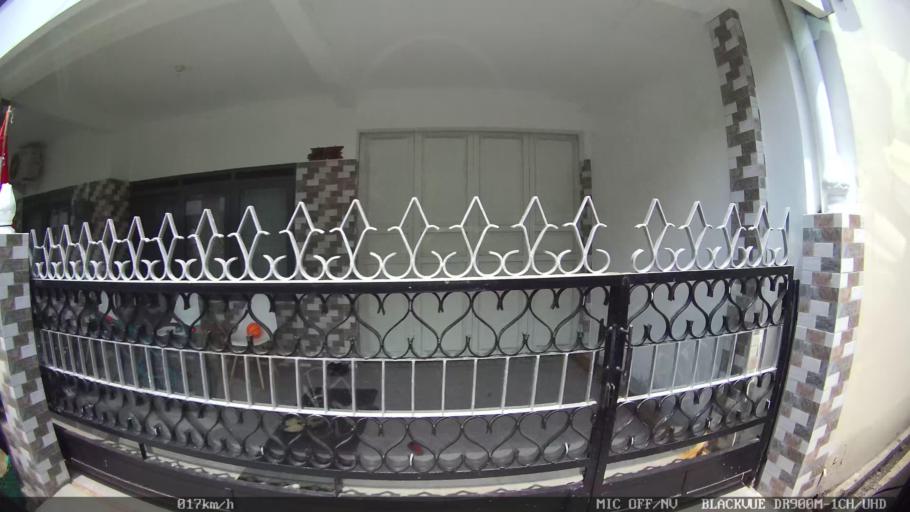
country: ID
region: Daerah Istimewa Yogyakarta
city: Yogyakarta
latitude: -7.8180
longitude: 110.3925
